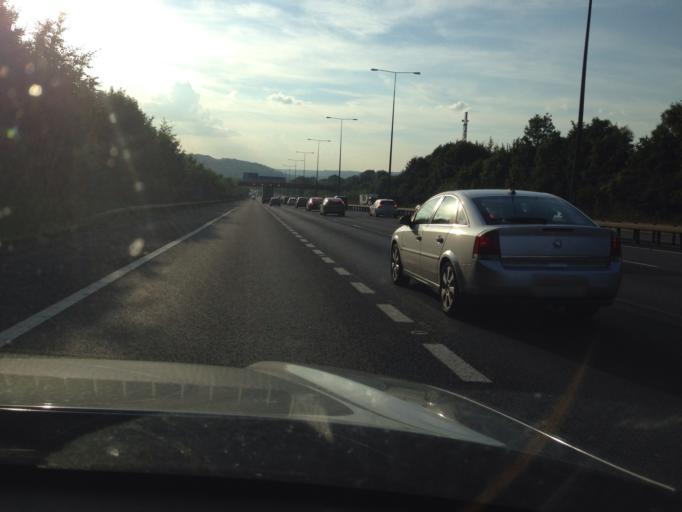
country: GB
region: England
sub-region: Buckinghamshire
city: Beaconsfield
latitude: 51.5991
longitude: -0.6789
